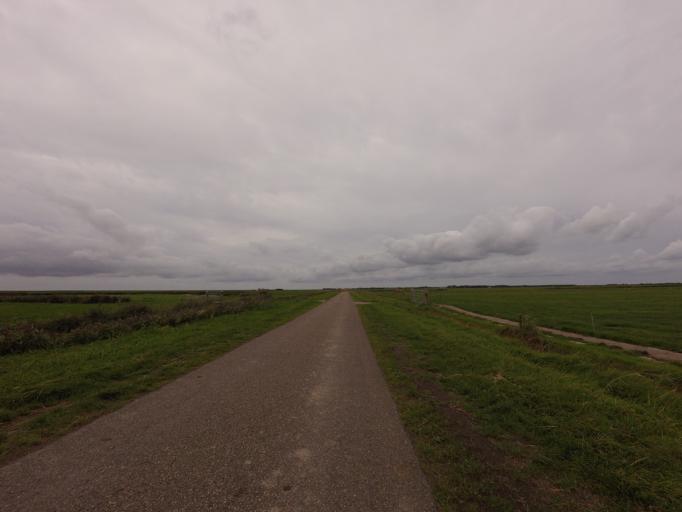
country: NL
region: Friesland
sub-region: Gemeente Ameland
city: Hollum
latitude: 53.4315
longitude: 5.6921
